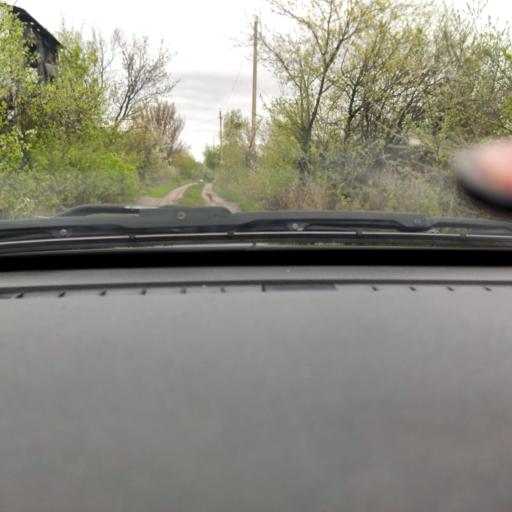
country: RU
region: Voronezj
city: Maslovka
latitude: 51.4915
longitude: 39.2166
